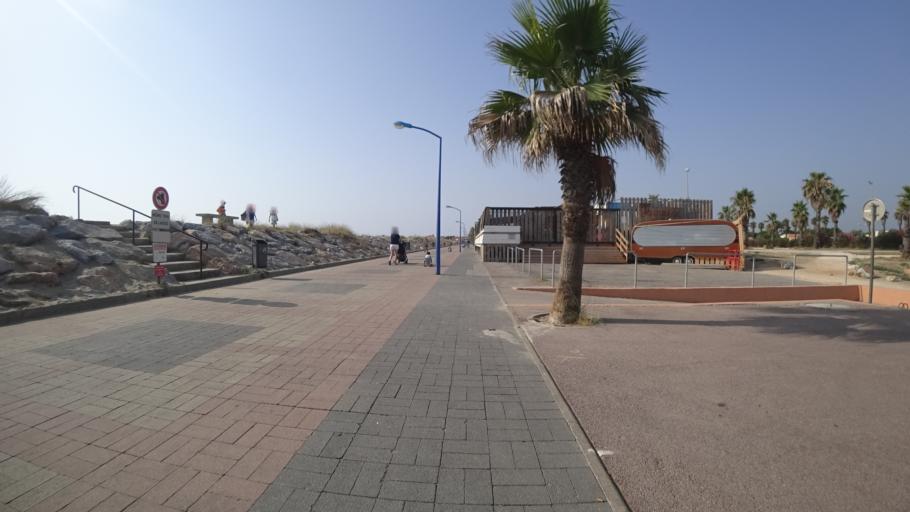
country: FR
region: Languedoc-Roussillon
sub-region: Departement des Pyrenees-Orientales
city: Sainte-Marie-Plage
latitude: 42.7330
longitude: 3.0371
